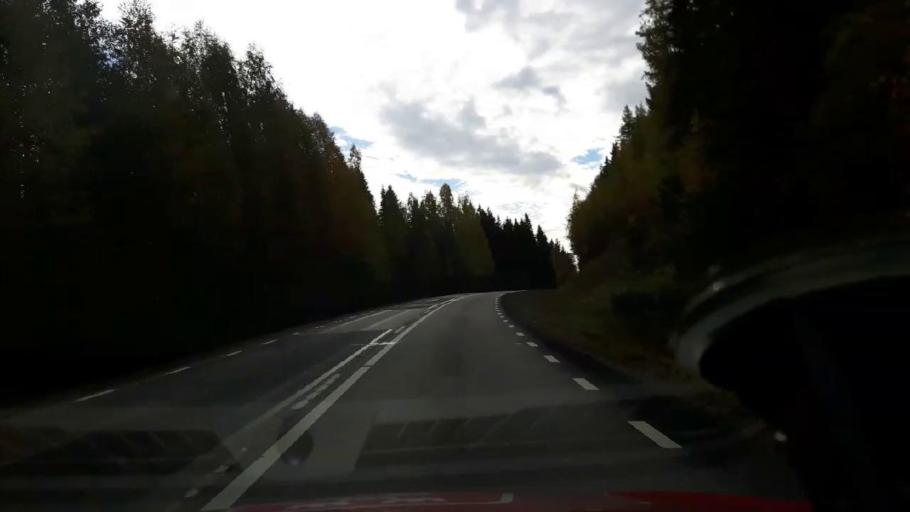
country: SE
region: Gaevleborg
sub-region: Ljusdals Kommun
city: Farila
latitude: 61.9543
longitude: 15.3647
